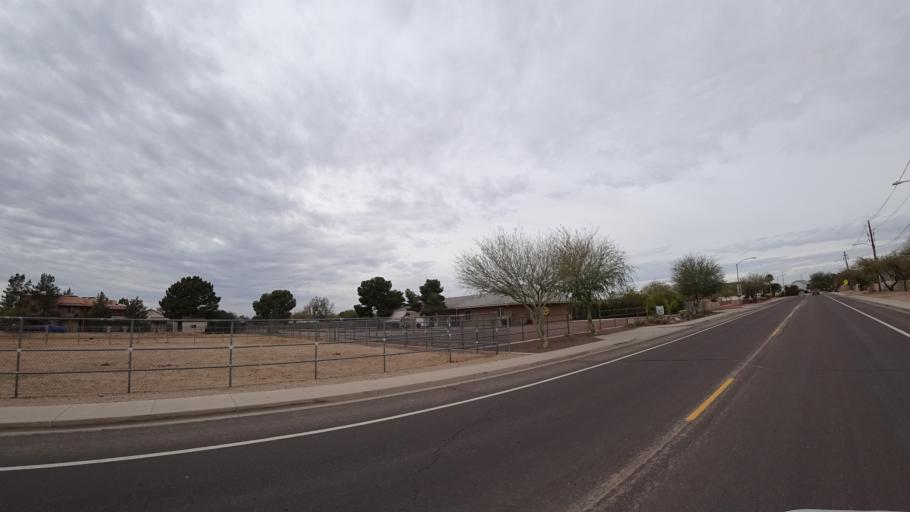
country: US
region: Arizona
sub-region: Maricopa County
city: Peoria
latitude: 33.6419
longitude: -112.1951
